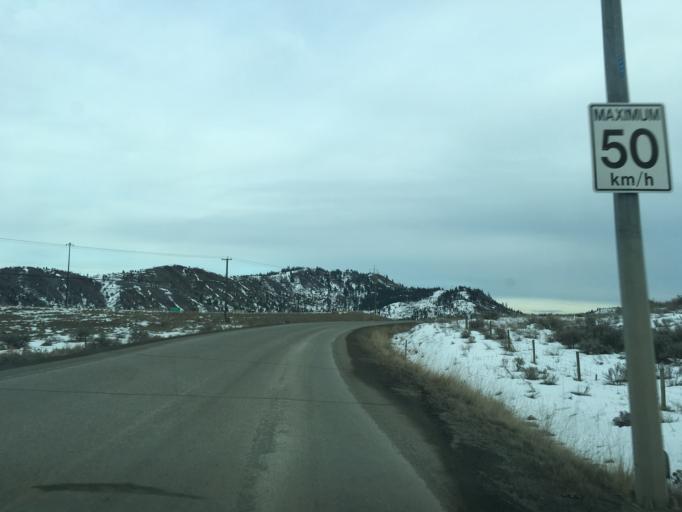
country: CA
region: British Columbia
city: Kamloops
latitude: 50.6646
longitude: -120.4279
